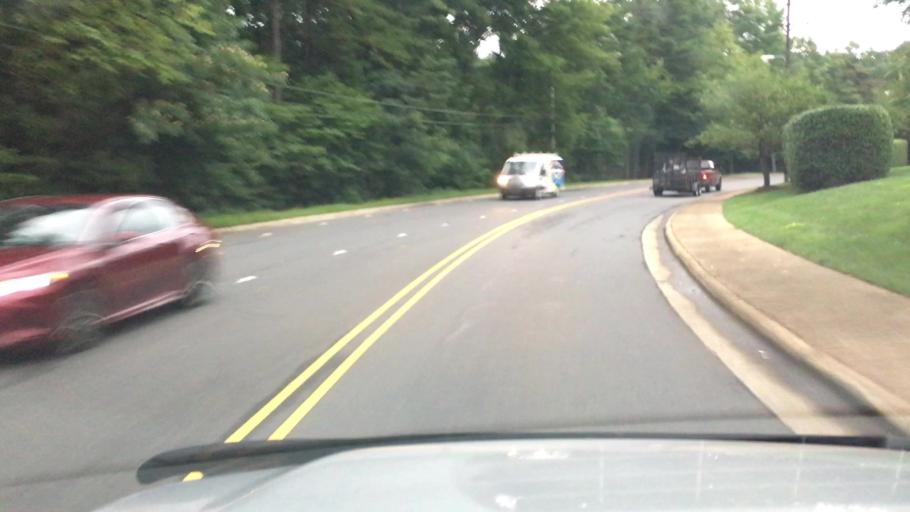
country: US
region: North Carolina
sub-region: Mecklenburg County
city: Matthews
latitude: 35.1377
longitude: -80.8019
